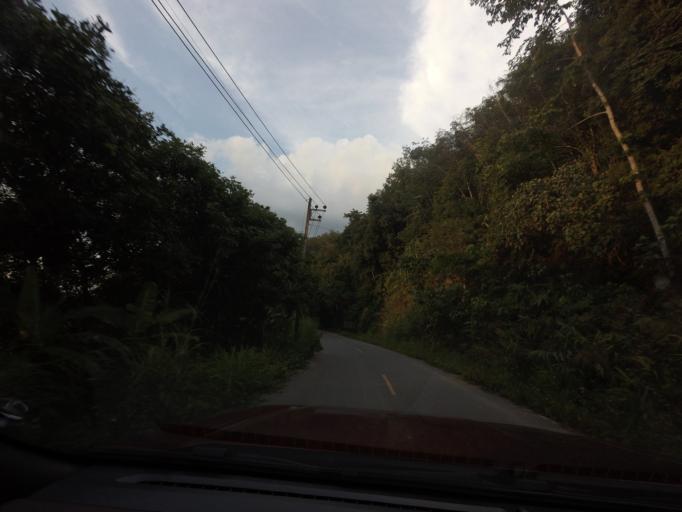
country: TH
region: Yala
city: Than To
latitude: 6.0087
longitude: 101.2283
